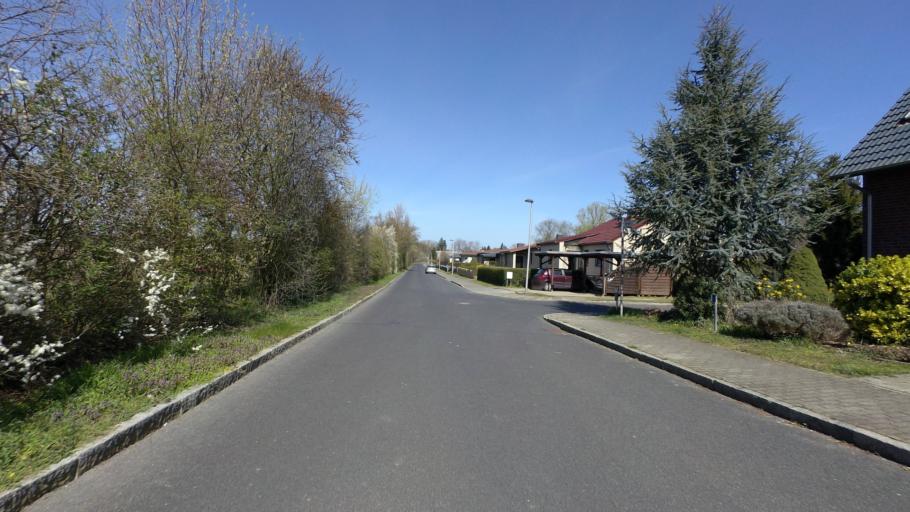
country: DE
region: Brandenburg
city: Rangsdorf
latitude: 52.3222
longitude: 13.4277
